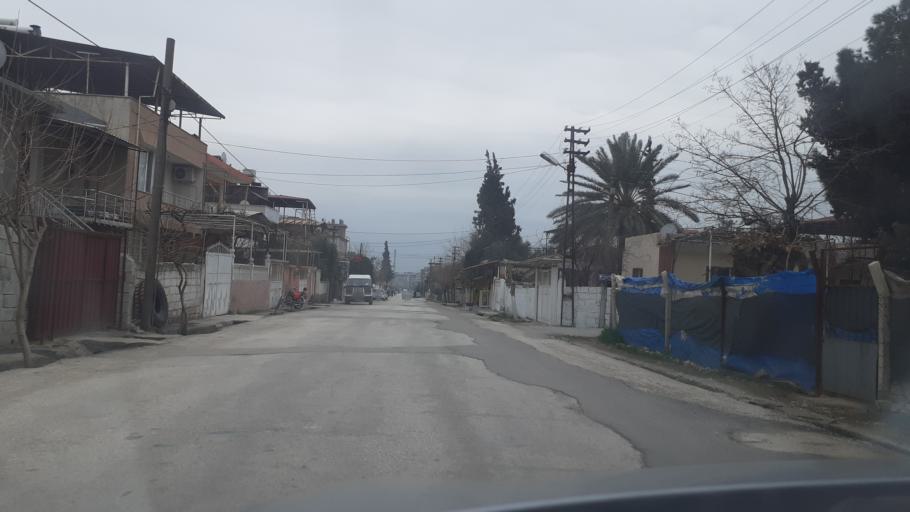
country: TR
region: Hatay
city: Kirikhan
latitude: 36.4896
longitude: 36.3558
